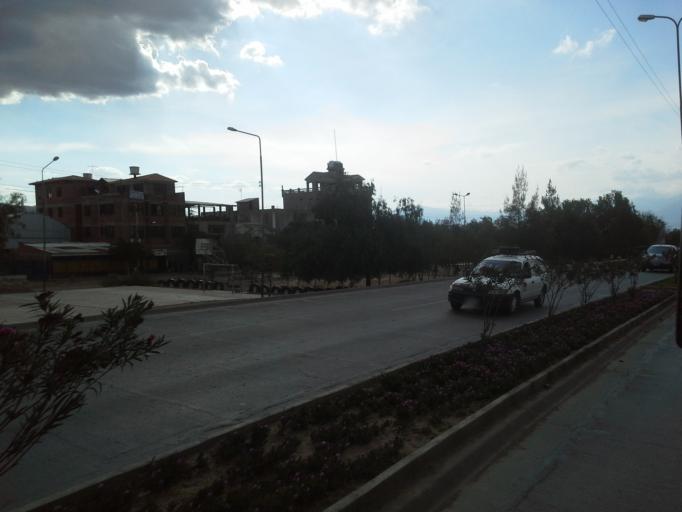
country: BO
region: Cochabamba
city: Cochabamba
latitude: -17.4444
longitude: -66.1398
